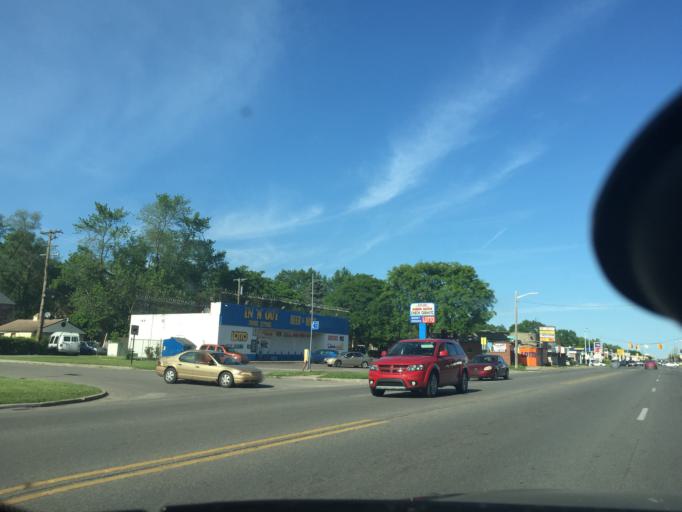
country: US
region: Michigan
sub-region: Oakland County
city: Southfield
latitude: 42.4152
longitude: -83.2343
